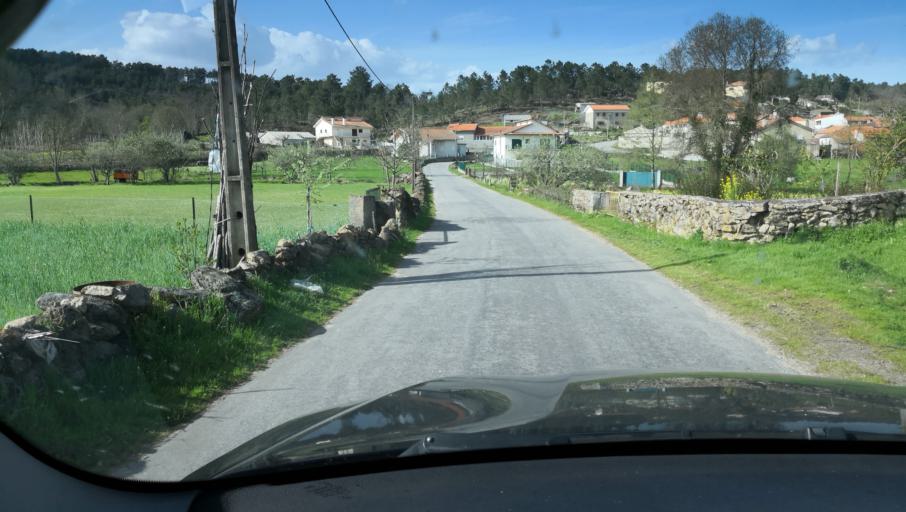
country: PT
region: Vila Real
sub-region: Vila Real
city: Vila Real
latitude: 41.2819
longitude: -7.6689
